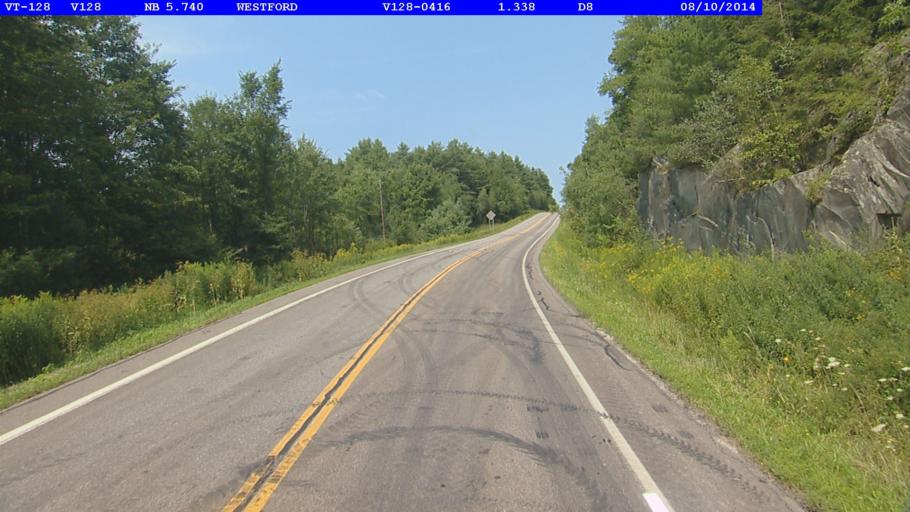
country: US
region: Vermont
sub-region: Chittenden County
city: Jericho
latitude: 44.5774
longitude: -73.0196
